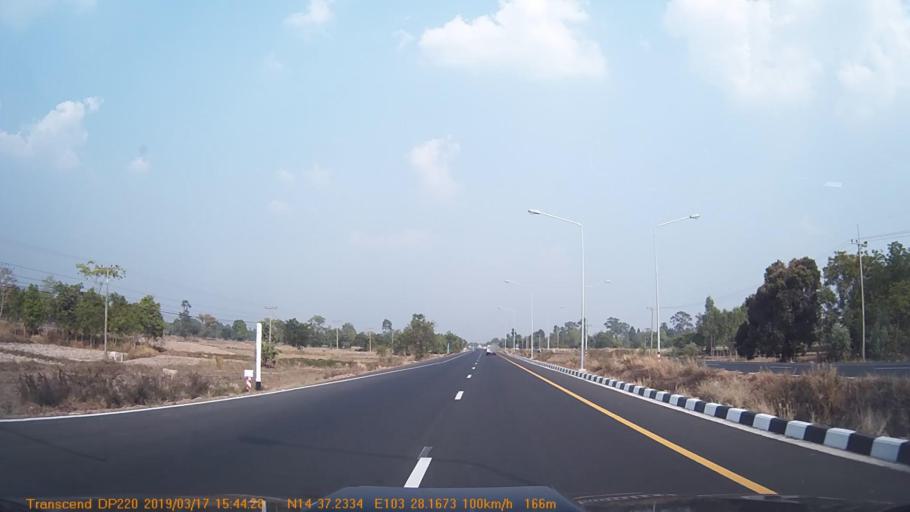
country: TH
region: Surin
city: Prasat
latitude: 14.6205
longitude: 103.4698
